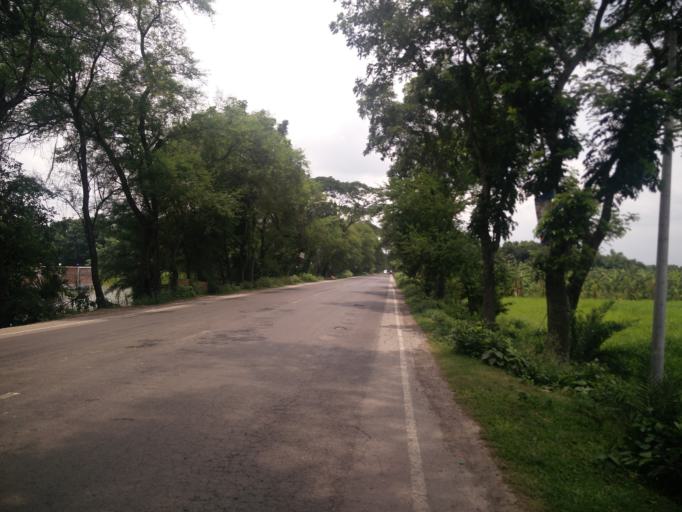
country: BD
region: Khulna
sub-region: Magura
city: Magura
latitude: 23.5445
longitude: 89.5309
